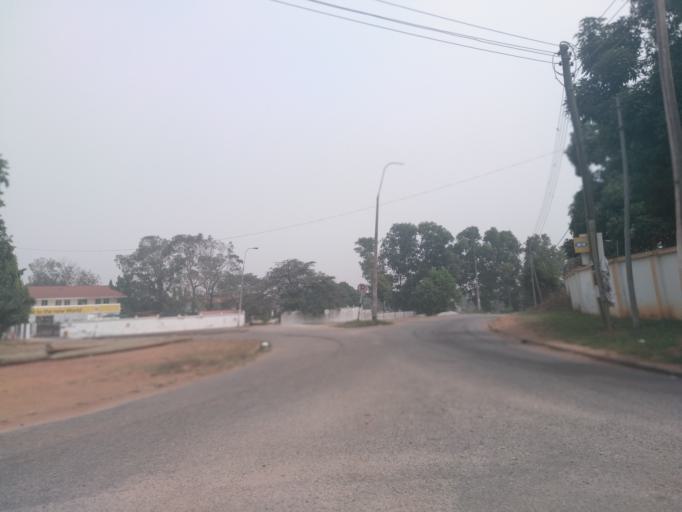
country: GH
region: Ashanti
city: Kumasi
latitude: 6.6765
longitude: -1.6195
